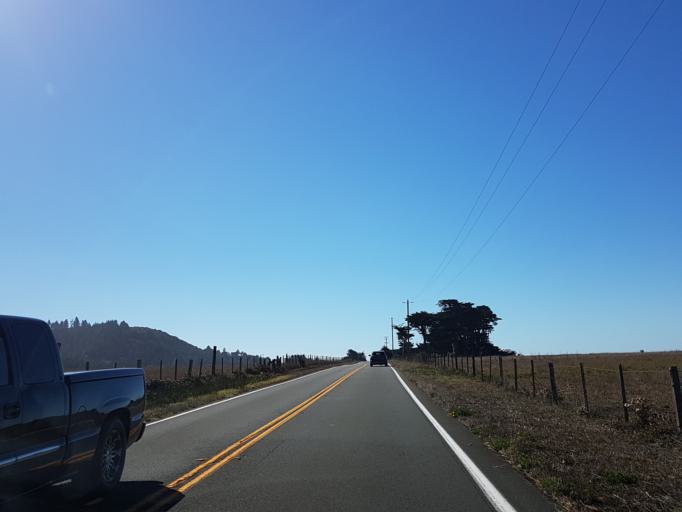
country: US
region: California
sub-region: Mendocino County
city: Boonville
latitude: 39.0446
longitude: -123.6854
